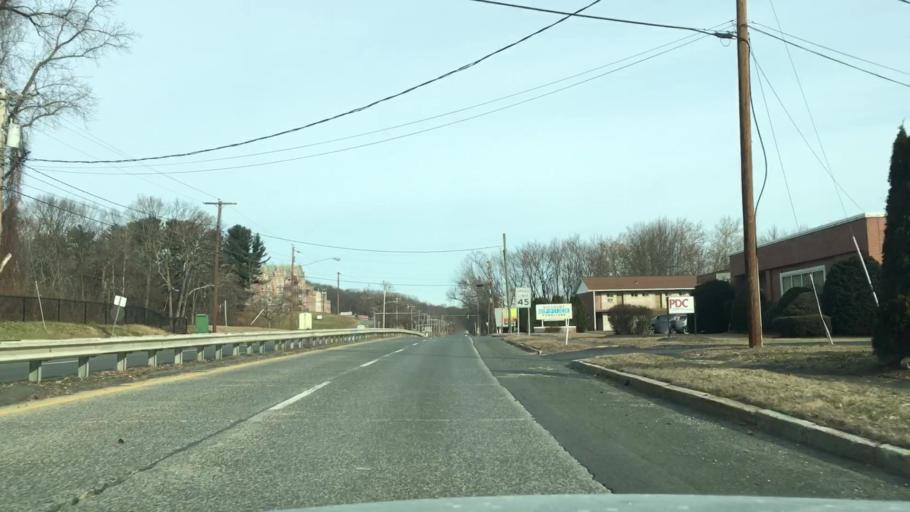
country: US
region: Massachusetts
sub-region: Hampden County
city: Chicopee
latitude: 42.1606
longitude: -72.6331
